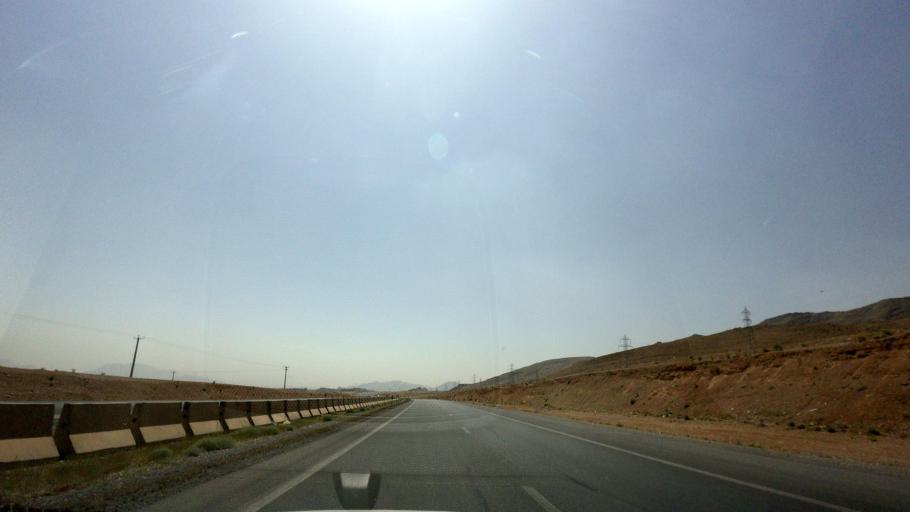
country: IR
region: Isfahan
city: Najafabad
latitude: 32.5419
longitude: 51.3140
